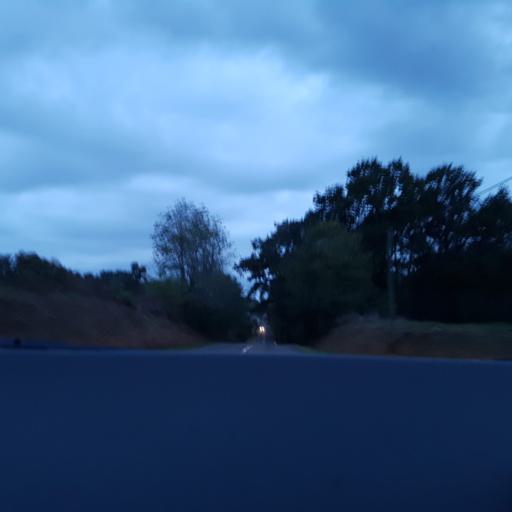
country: FR
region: Aquitaine
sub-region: Departement des Landes
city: Gabarret
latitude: 43.9471
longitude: 0.0245
